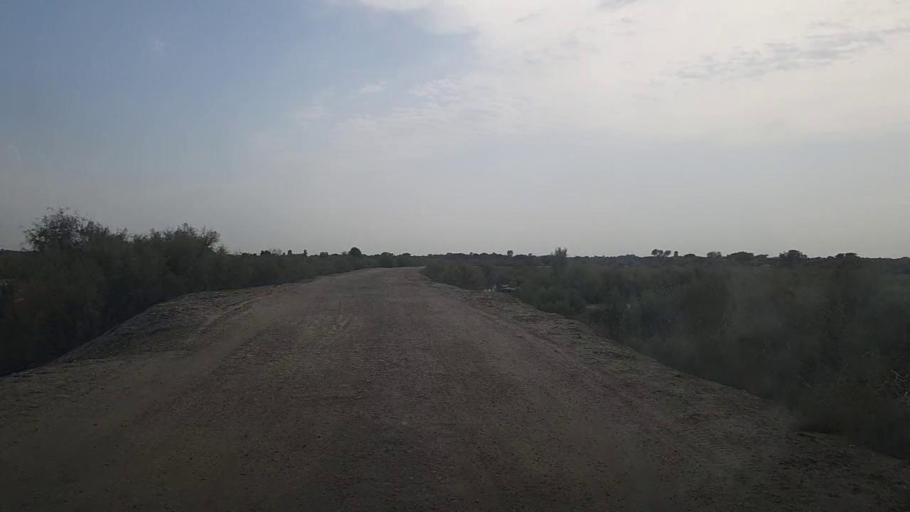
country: PK
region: Sindh
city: Mirpur Mathelo
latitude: 27.9147
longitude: 69.5142
